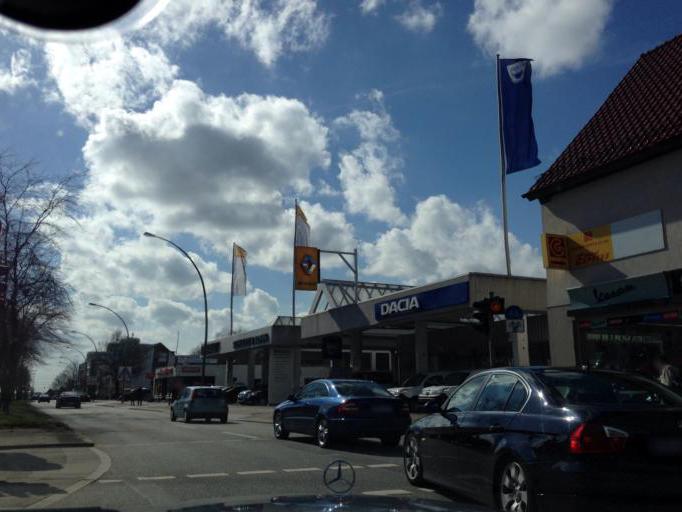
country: DE
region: Hamburg
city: Wandsbek
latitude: 53.5434
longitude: 10.1035
